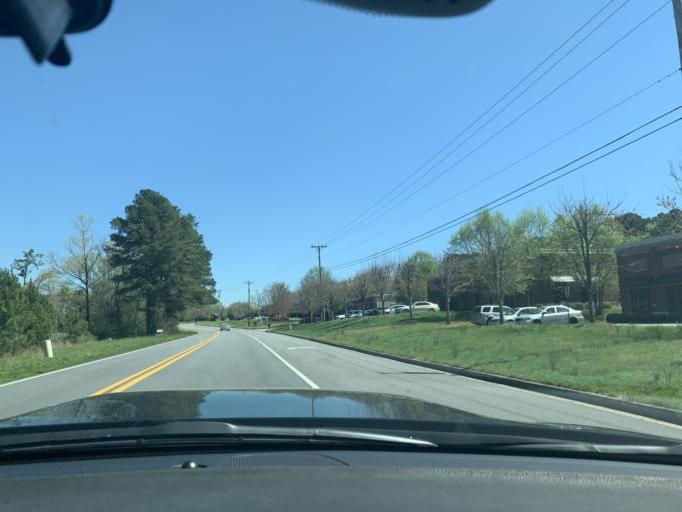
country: US
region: Georgia
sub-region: Fulton County
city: Milton
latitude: 34.1332
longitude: -84.2096
